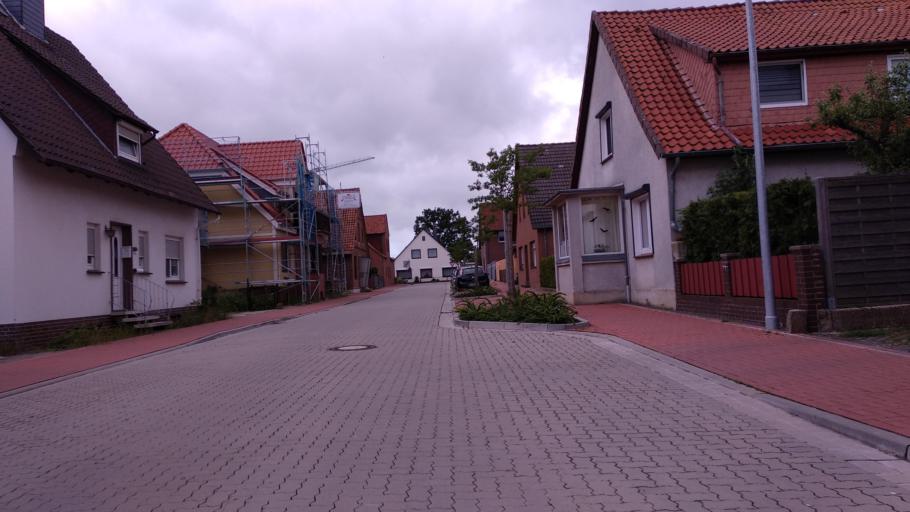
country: DE
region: Lower Saxony
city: Hagenburg
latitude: 52.4530
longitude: 9.3627
